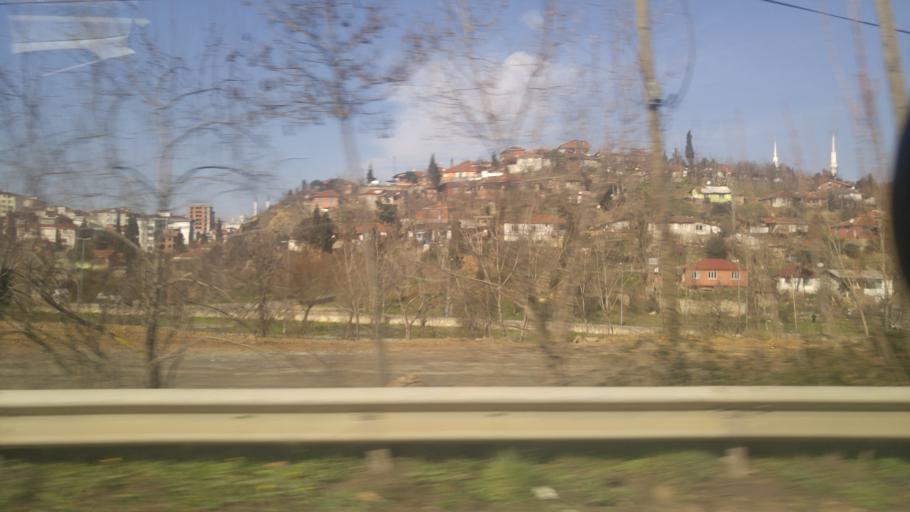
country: TR
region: Kocaeli
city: Darica
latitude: 40.8327
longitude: 29.3694
